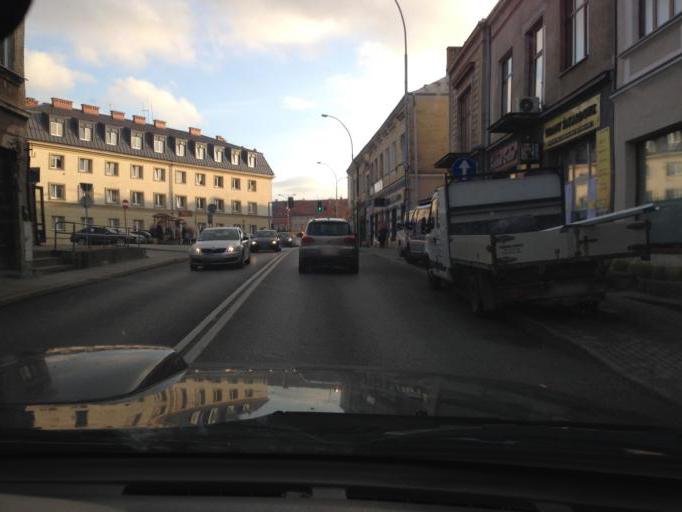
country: PL
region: Subcarpathian Voivodeship
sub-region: Powiat jasielski
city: Jaslo
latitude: 49.7484
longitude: 21.4734
